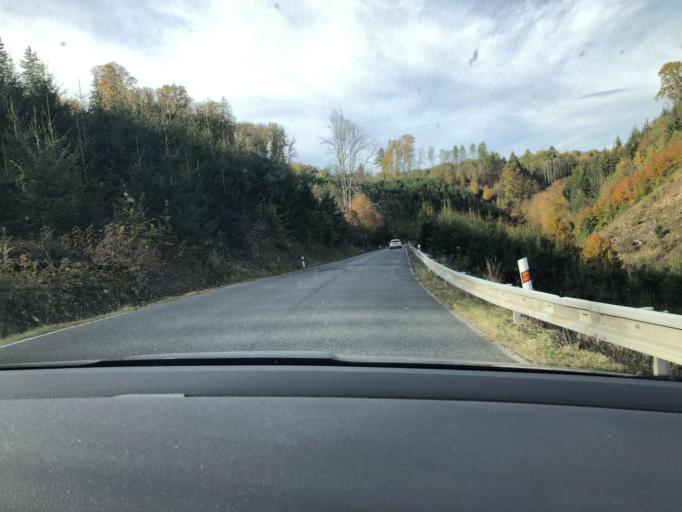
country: CZ
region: Central Bohemia
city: Divisov
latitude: 49.8037
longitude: 14.9261
